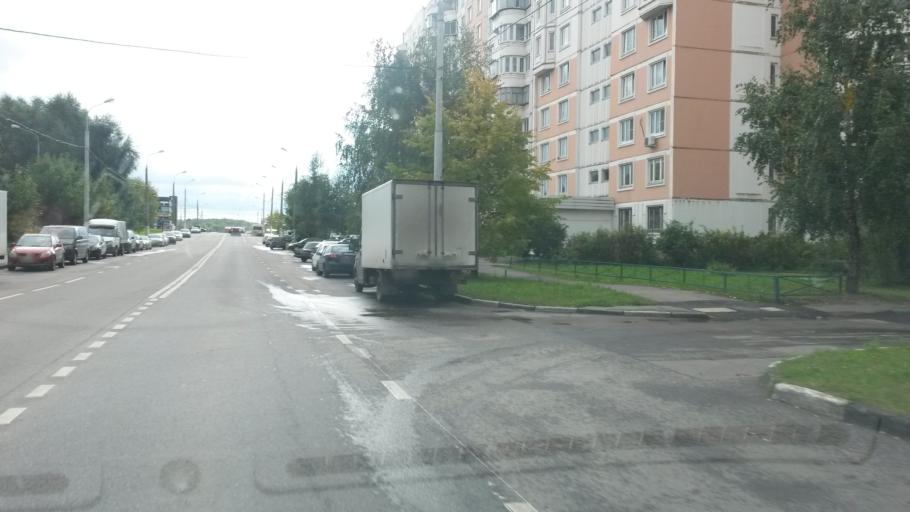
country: RU
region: Moskovskaya
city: Kommunarka
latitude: 55.5313
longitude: 37.5187
